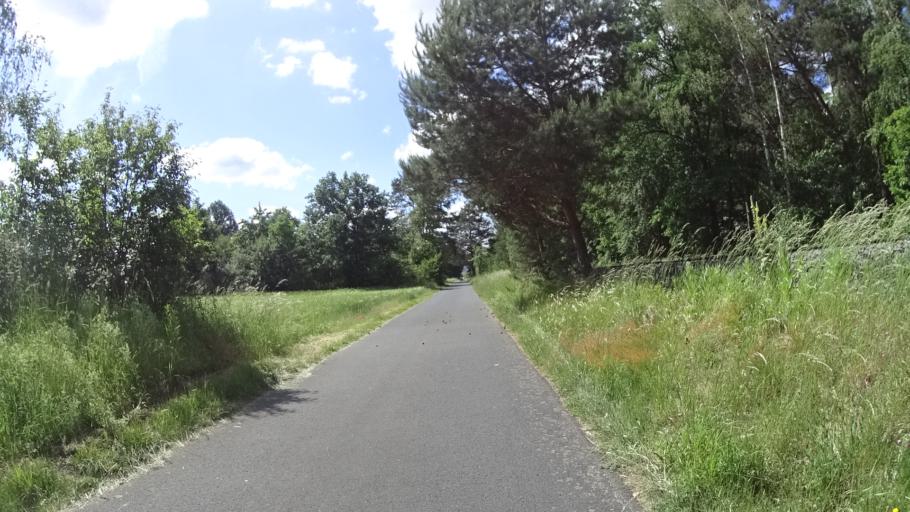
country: DE
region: Bavaria
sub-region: Regierungsbezirk Unterfranken
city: Erlenbach am Main
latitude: 49.8135
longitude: 9.1538
